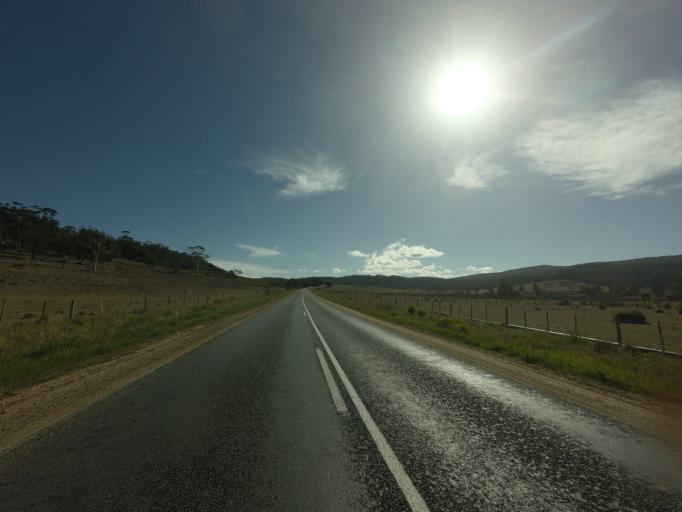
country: AU
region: Tasmania
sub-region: Break O'Day
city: St Helens
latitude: -41.9557
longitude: 148.1742
